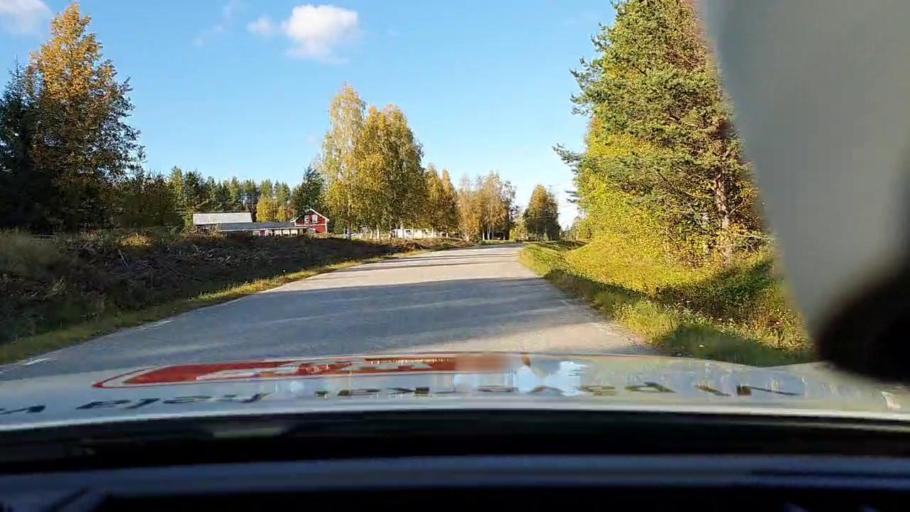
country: SE
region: Norrbotten
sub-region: Pitea Kommun
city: Norrfjarden
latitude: 65.5272
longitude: 21.4873
